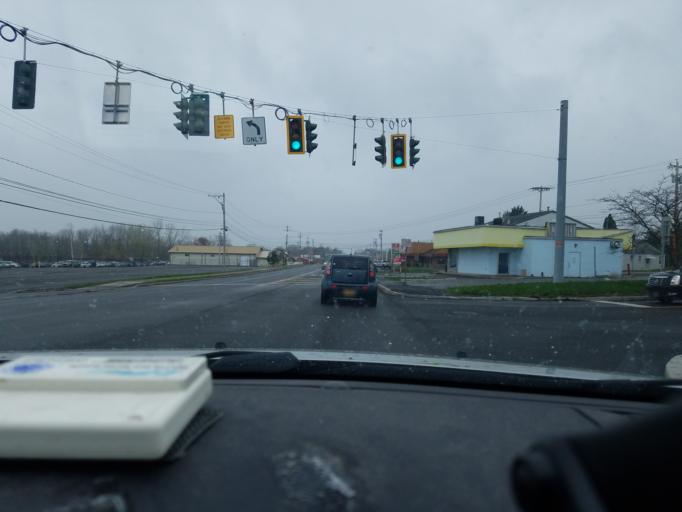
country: US
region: New York
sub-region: Onondaga County
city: North Syracuse
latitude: 43.1759
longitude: -76.1097
